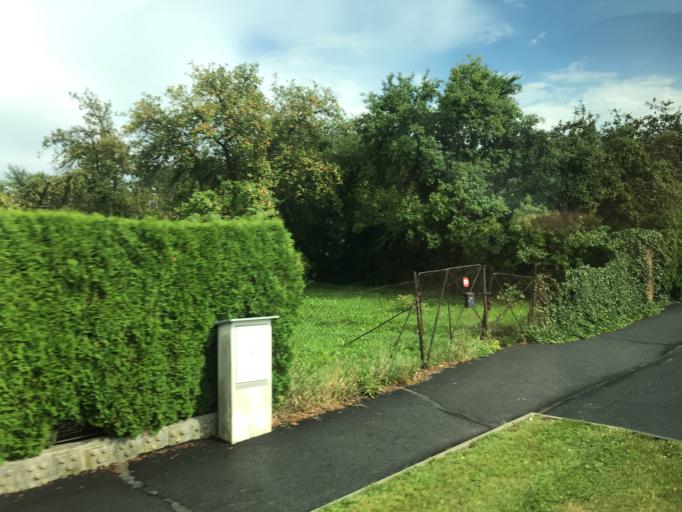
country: CZ
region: Jihocesky
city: Vcelna
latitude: 48.9198
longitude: 14.4526
